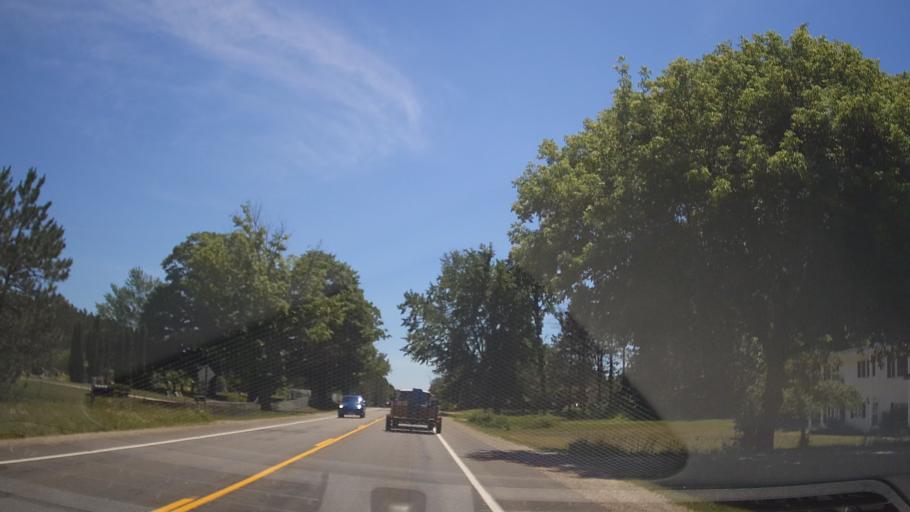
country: US
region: Michigan
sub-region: Grand Traverse County
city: Traverse City
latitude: 44.6519
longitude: -85.6965
